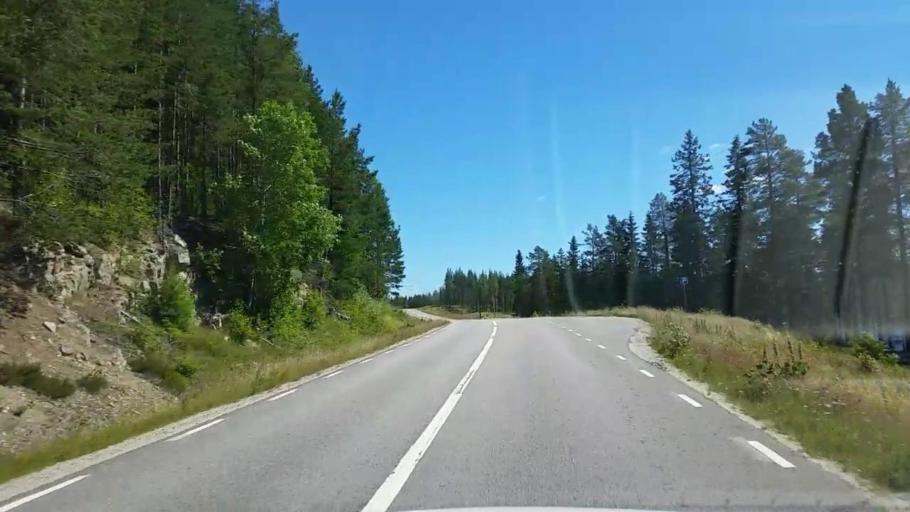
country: SE
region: Gaevleborg
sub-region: Ovanakers Kommun
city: Edsbyn
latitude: 61.5915
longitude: 15.6189
